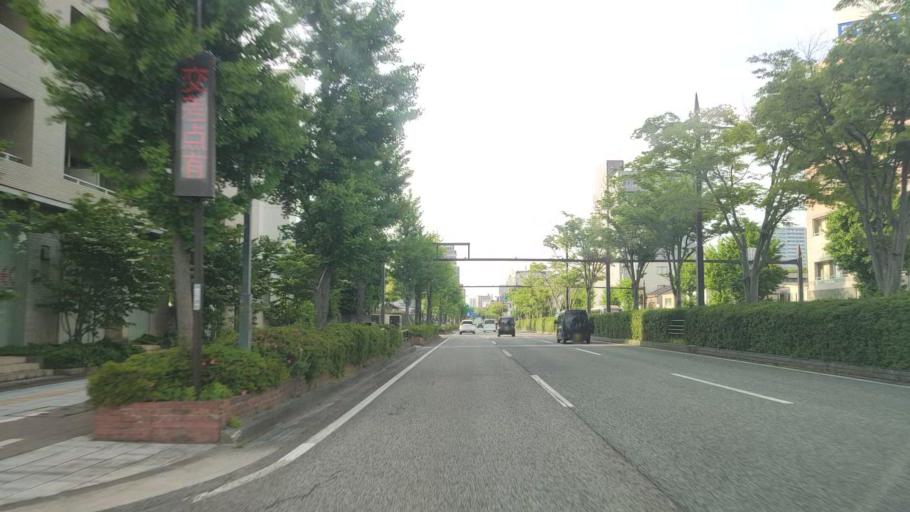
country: JP
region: Toyama
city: Toyama-shi
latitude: 36.6846
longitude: 137.2118
